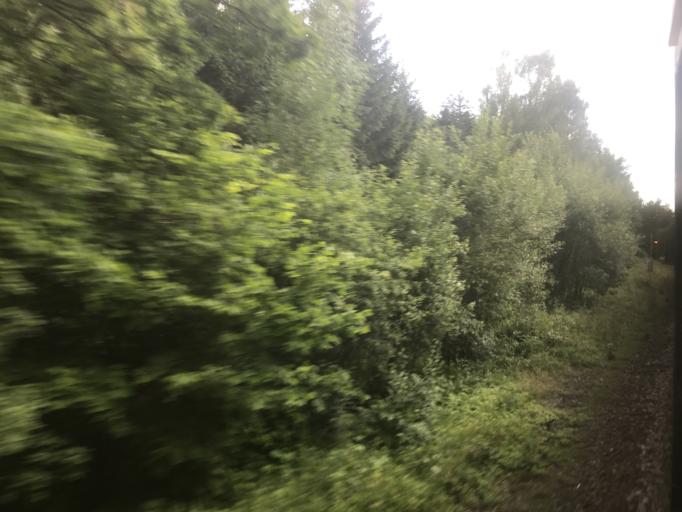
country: CZ
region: Jihocesky
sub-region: Okres Cesky Krumlov
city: Dolni Dvoriste
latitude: 48.6384
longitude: 14.4213
